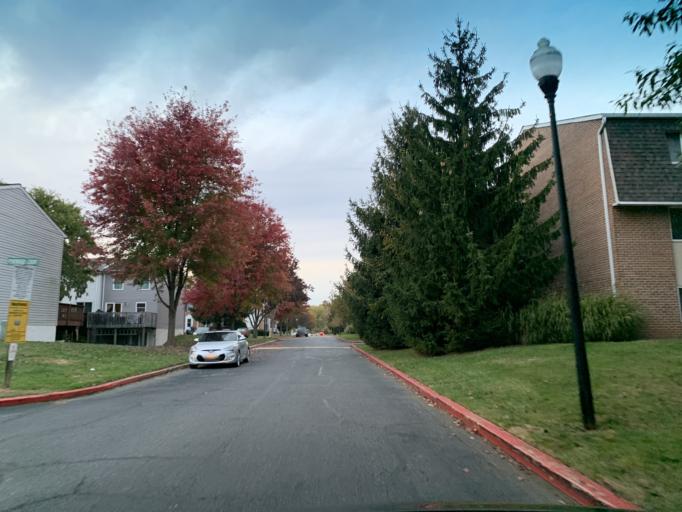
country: US
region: Maryland
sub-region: Harford County
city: South Bel Air
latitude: 39.5402
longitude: -76.3276
